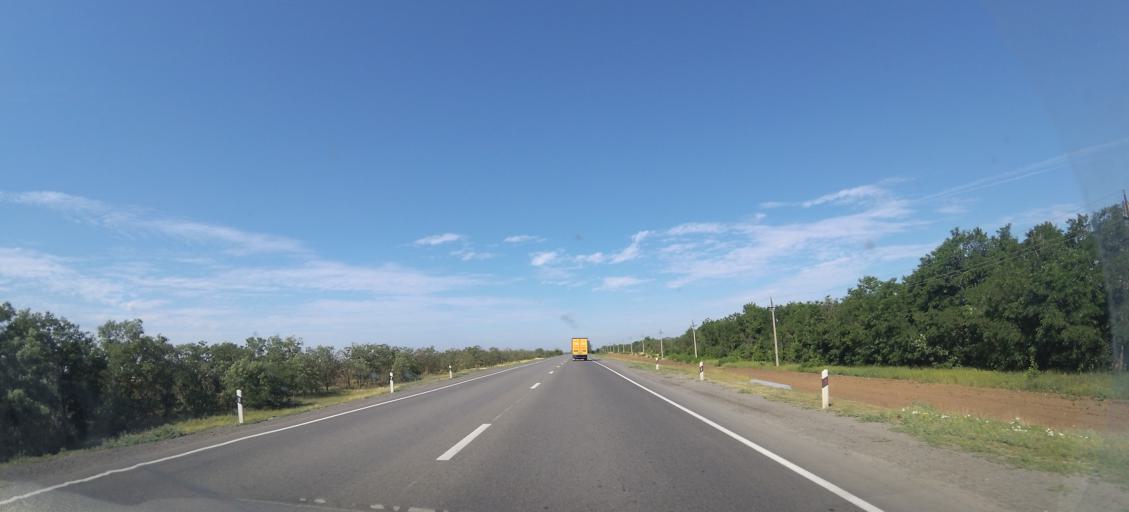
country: RU
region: Volgograd
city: Oktyabr'skiy
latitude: 48.6963
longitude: 43.7971
